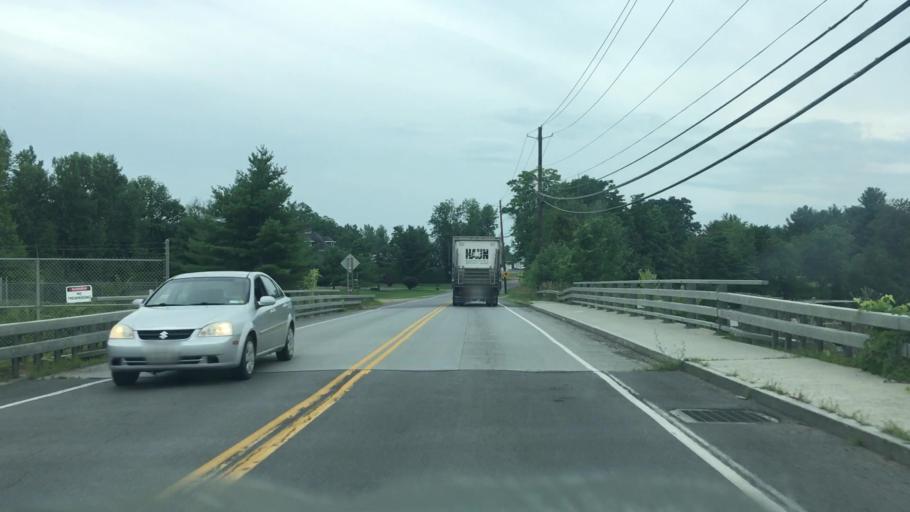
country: US
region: New York
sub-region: Clinton County
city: Plattsburgh West
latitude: 44.6687
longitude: -73.5076
